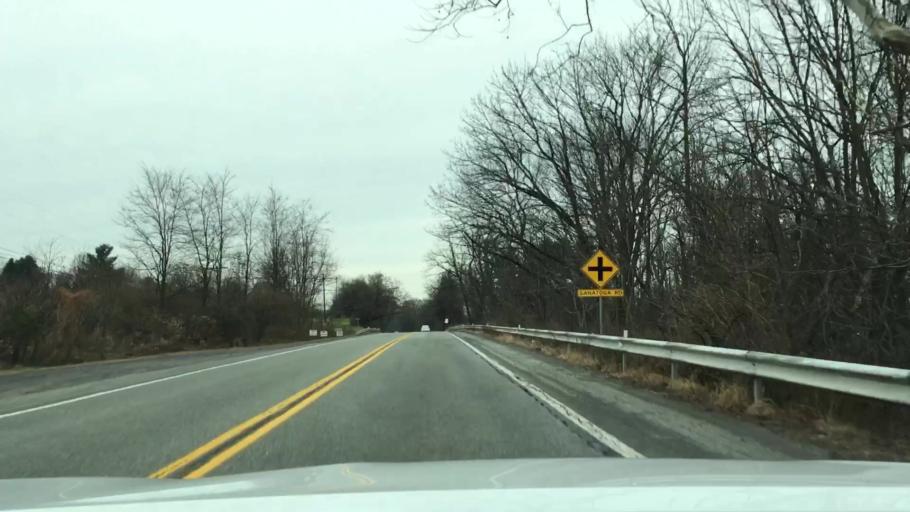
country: US
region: Pennsylvania
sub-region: Montgomery County
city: Sanatoga
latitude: 40.2120
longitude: -75.5988
